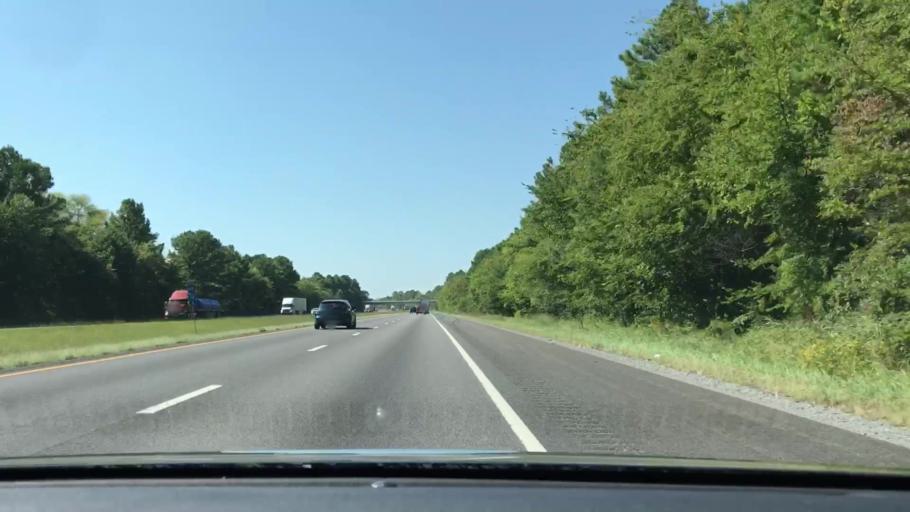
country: US
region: Tennessee
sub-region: Sumner County
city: White House
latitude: 36.5039
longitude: -86.6630
